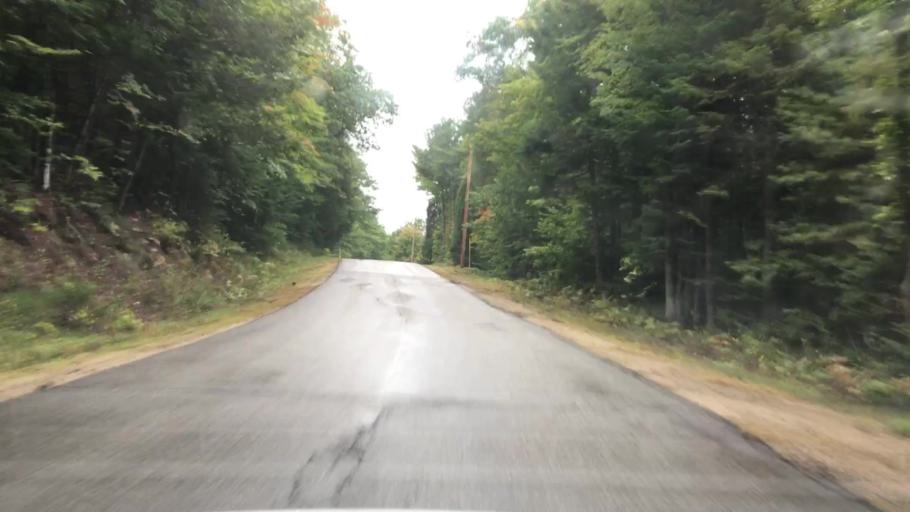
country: US
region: Maine
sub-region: Cumberland County
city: Harrison
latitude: 44.0315
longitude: -70.5986
